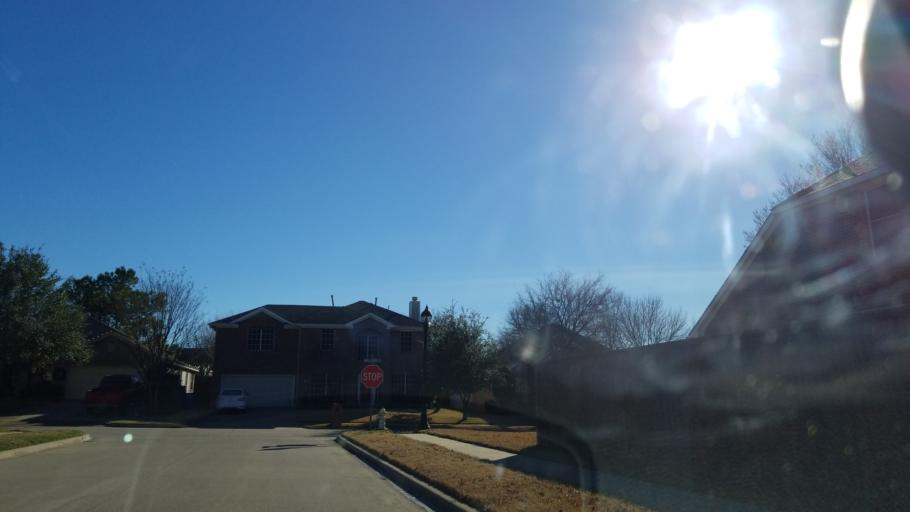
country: US
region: Texas
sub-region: Denton County
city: Corinth
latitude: 33.1373
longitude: -97.0855
